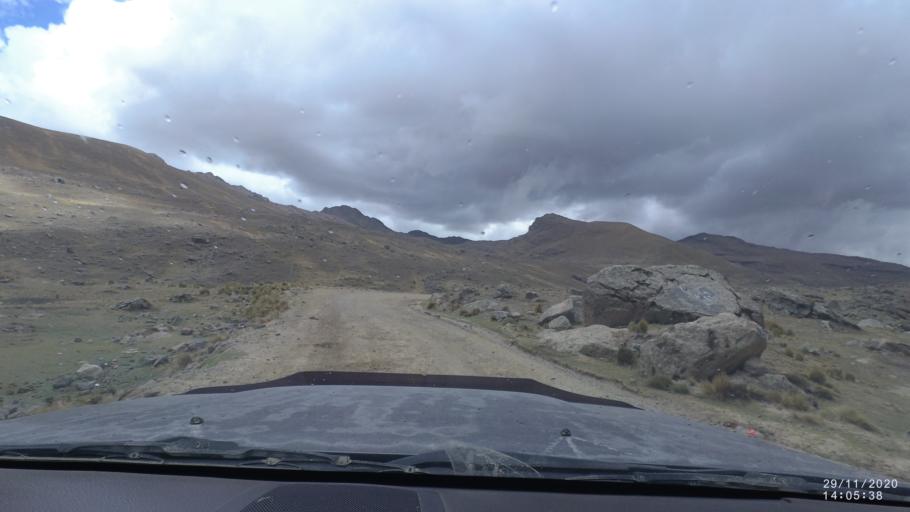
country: BO
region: Cochabamba
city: Sipe Sipe
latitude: -17.2080
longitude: -66.3767
